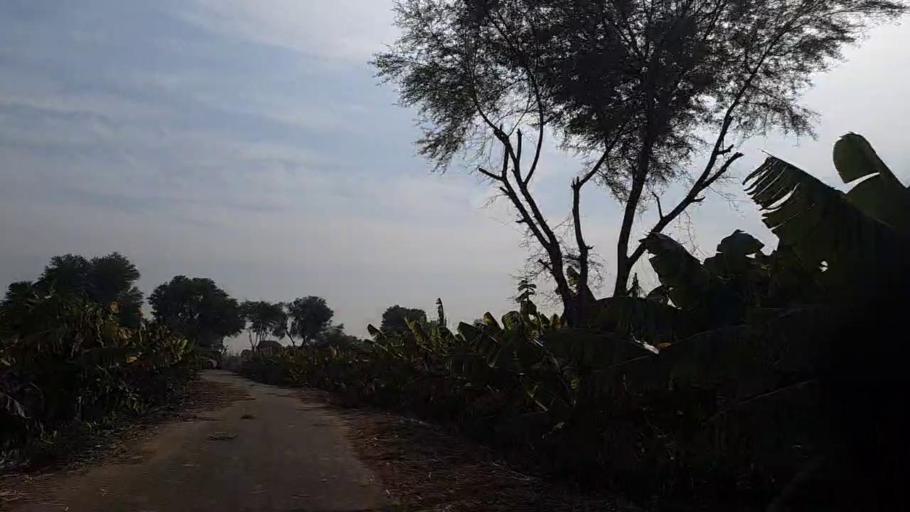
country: PK
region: Sindh
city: Daur
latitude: 26.3939
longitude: 68.2014
